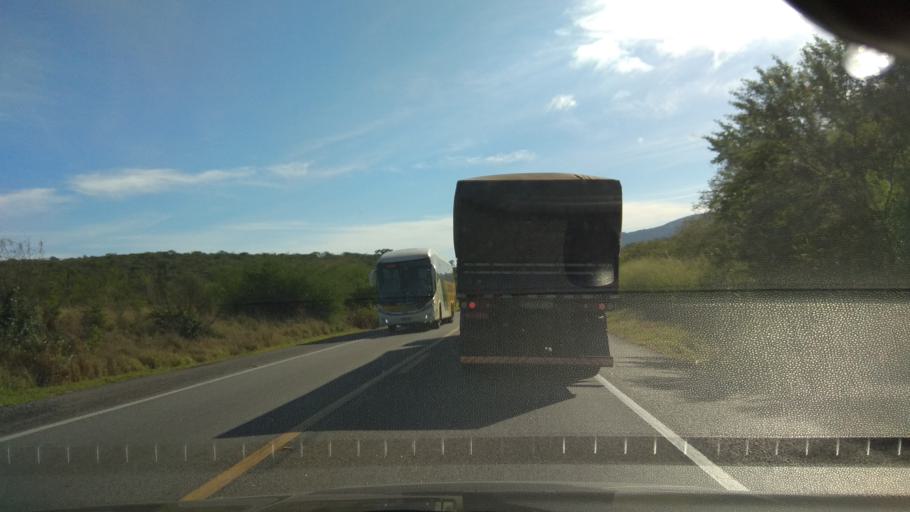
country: BR
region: Bahia
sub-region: Jequie
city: Jequie
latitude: -13.7670
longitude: -40.1022
